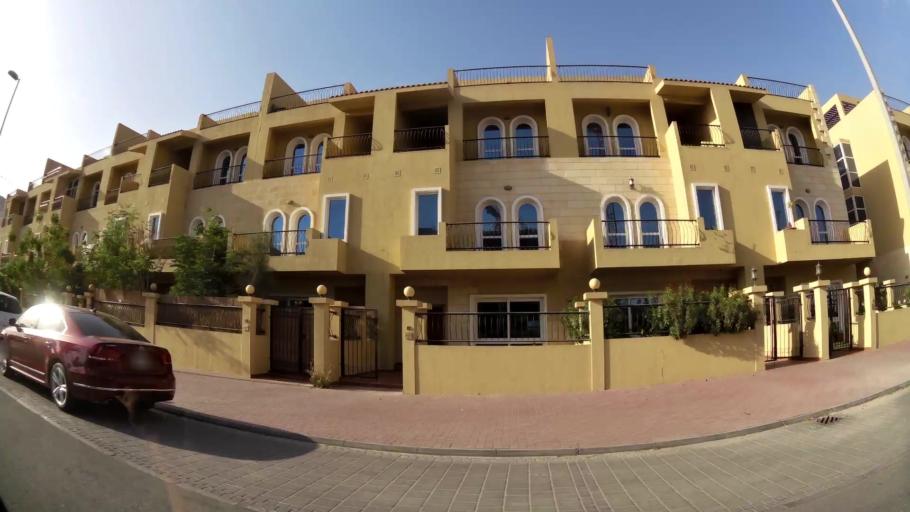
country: AE
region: Dubai
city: Dubai
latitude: 25.0502
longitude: 55.2048
